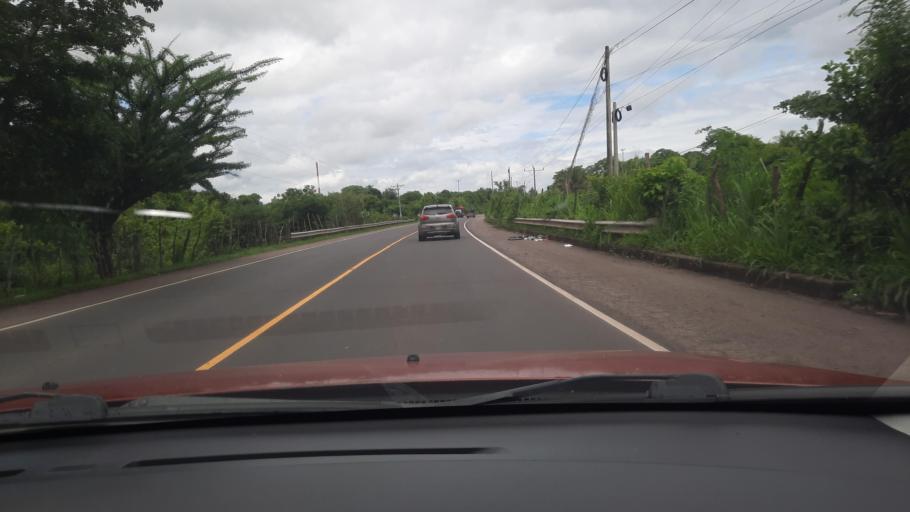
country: SV
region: Ahuachapan
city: Guaymango
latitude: 13.6987
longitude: -89.9473
